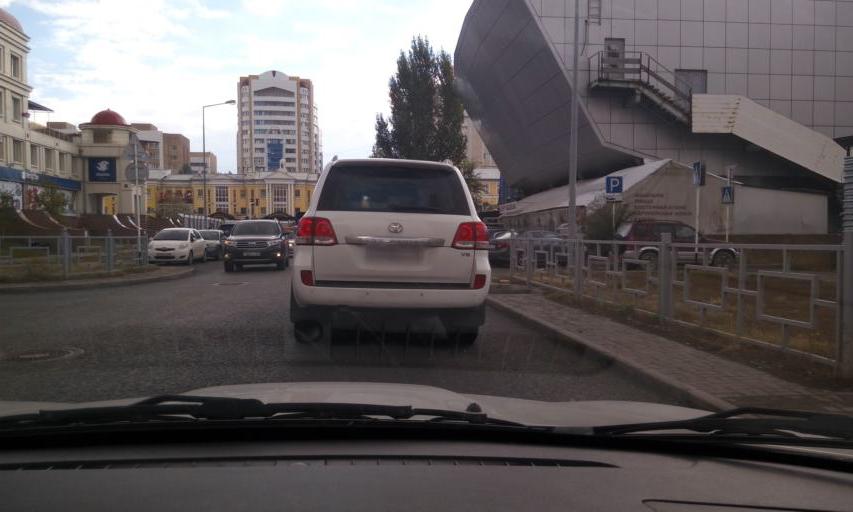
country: KZ
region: Astana Qalasy
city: Astana
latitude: 51.1644
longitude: 71.4319
